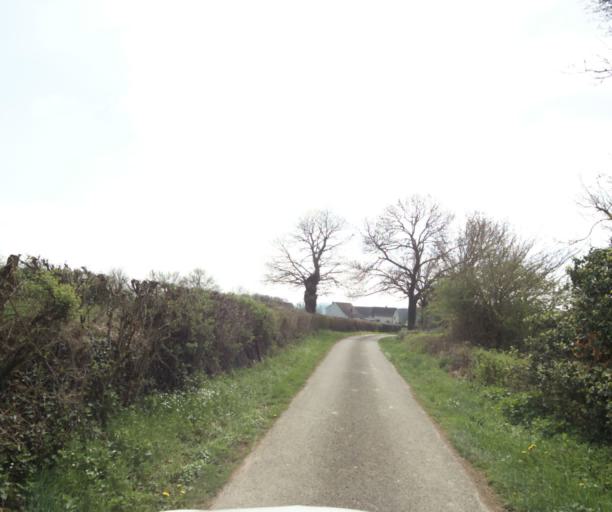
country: FR
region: Bourgogne
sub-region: Departement de Saone-et-Loire
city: Charolles
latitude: 46.3750
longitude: 4.3065
